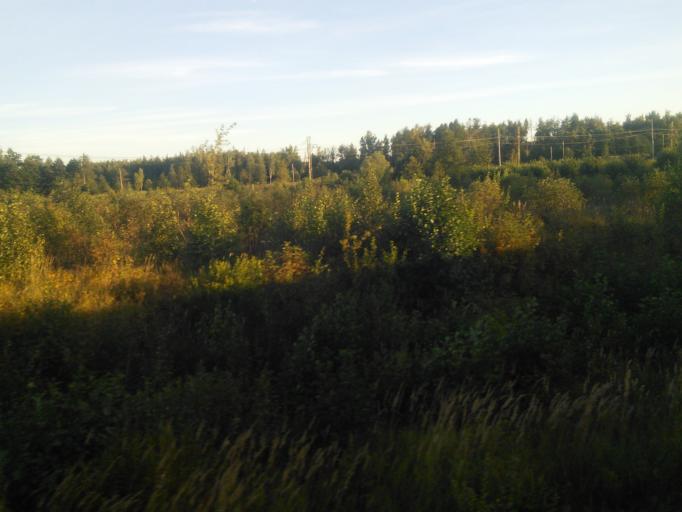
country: RU
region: Moskovskaya
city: Fryazevo
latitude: 55.7378
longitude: 38.4834
